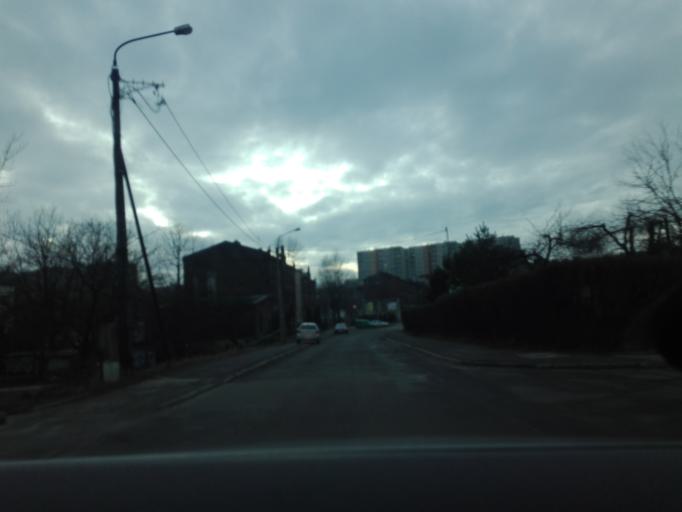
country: PL
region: Silesian Voivodeship
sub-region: Katowice
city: Katowice
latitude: 50.2856
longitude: 19.0170
